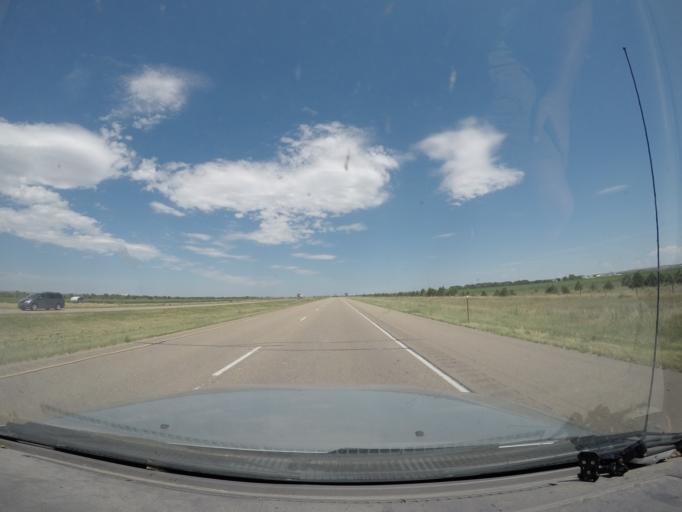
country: US
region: Colorado
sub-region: Sedgwick County
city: Julesburg
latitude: 41.0416
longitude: -102.0986
